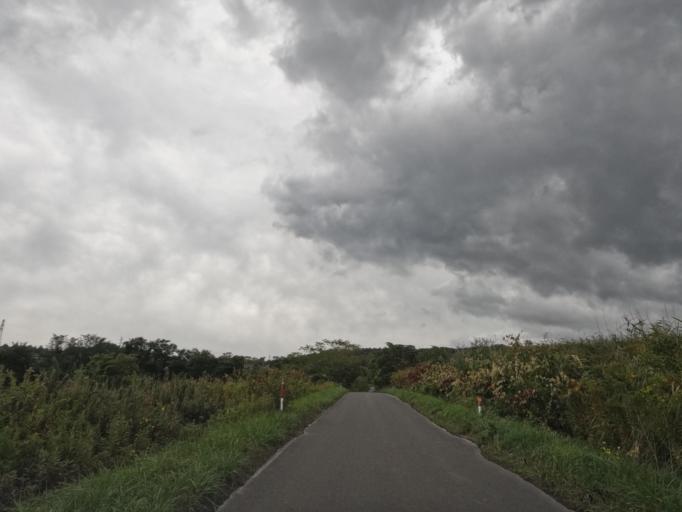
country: JP
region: Hokkaido
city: Date
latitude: 42.5044
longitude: 140.8911
